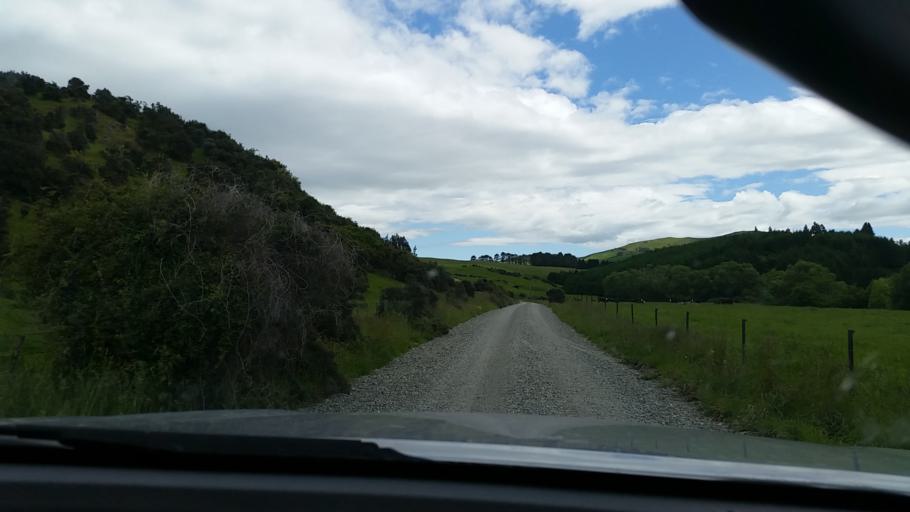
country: NZ
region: Otago
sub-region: Queenstown-Lakes District
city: Kingston
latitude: -45.7252
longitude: 168.5488
